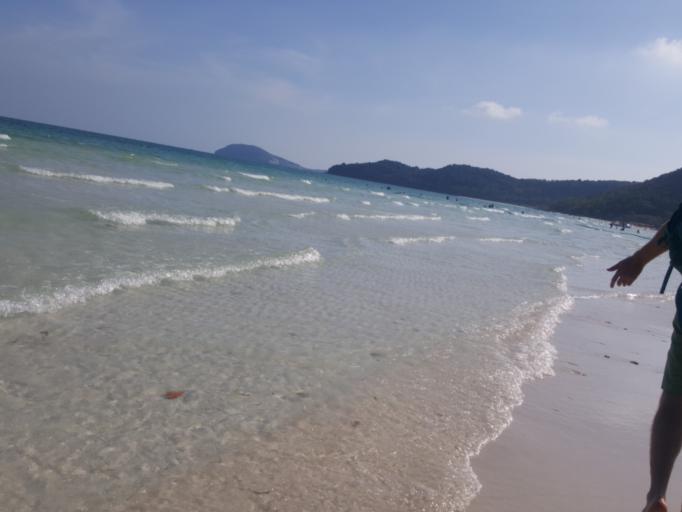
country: VN
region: Kien Giang
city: Duong GJong
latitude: 10.0583
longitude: 104.0370
